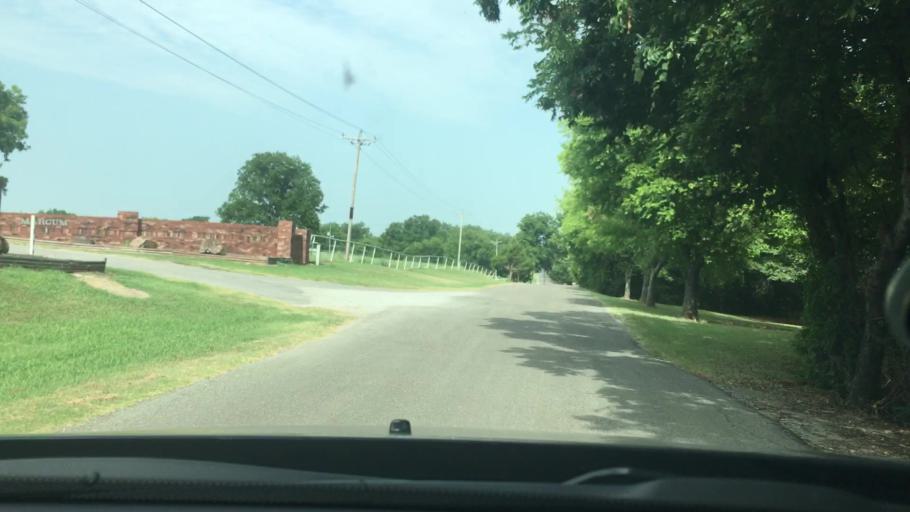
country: US
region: Oklahoma
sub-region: Garvin County
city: Pauls Valley
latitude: 34.7968
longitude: -97.1868
